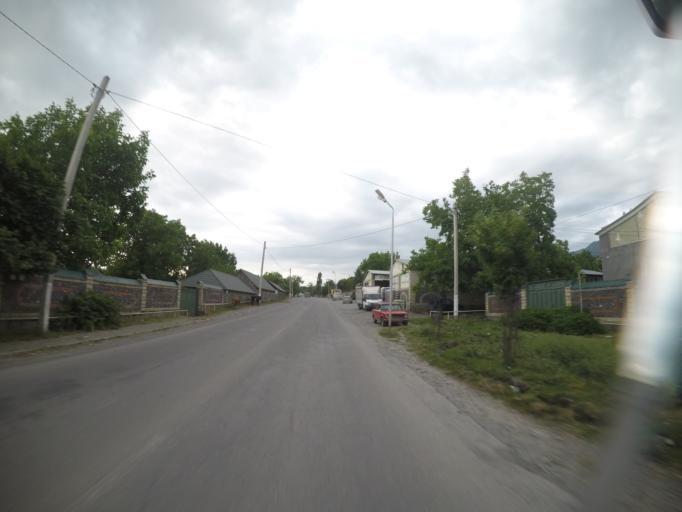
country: AZ
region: Qabala Rayon
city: Qutqashen
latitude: 40.9475
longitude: 47.9401
